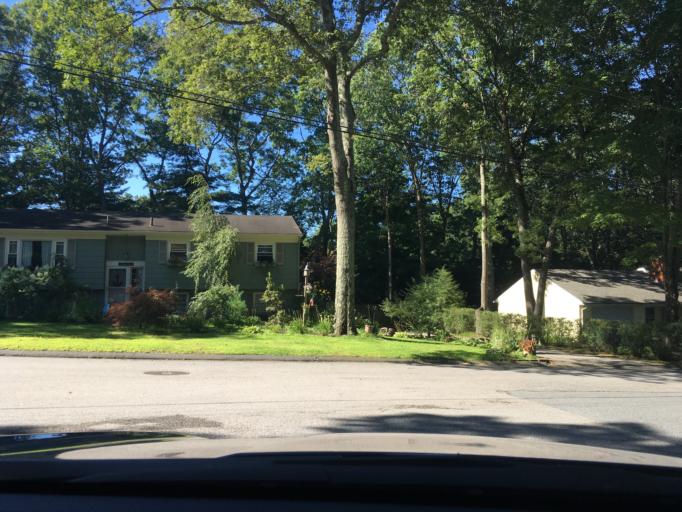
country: US
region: Rhode Island
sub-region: Kent County
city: East Greenwich
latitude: 41.6412
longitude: -71.4738
